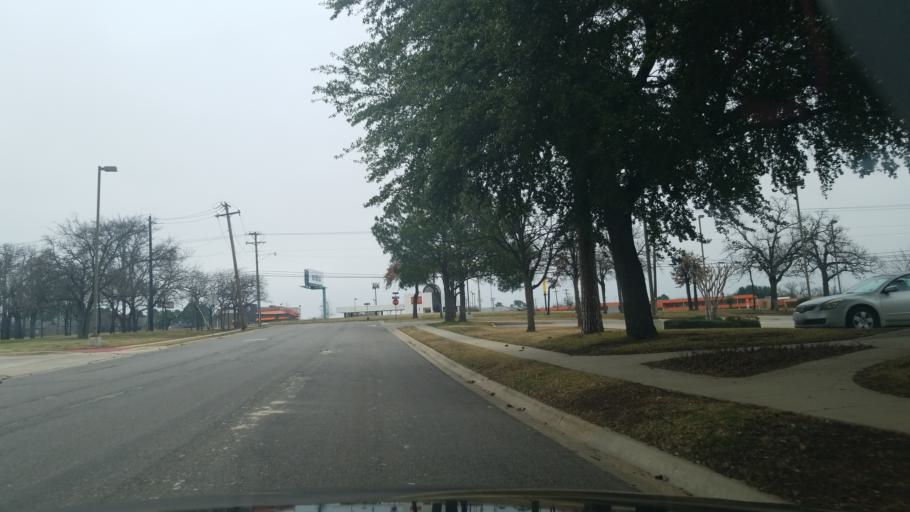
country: US
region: Texas
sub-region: Denton County
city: Denton
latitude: 33.1912
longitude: -97.1192
